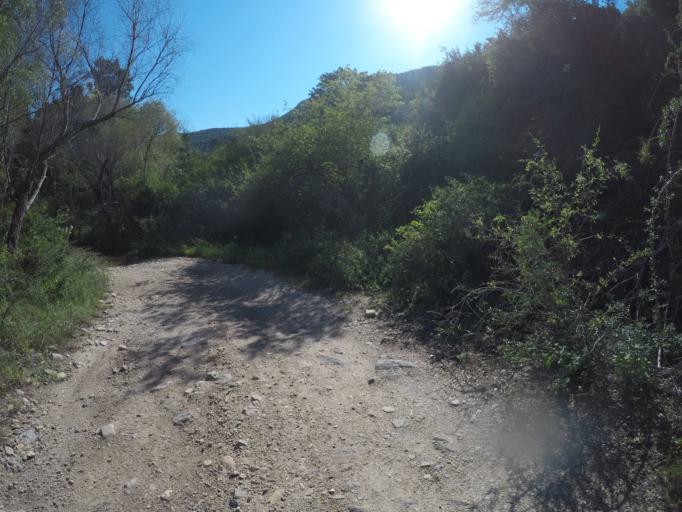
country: ZA
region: Eastern Cape
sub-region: Cacadu District Municipality
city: Kareedouw
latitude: -33.6528
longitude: 24.4191
